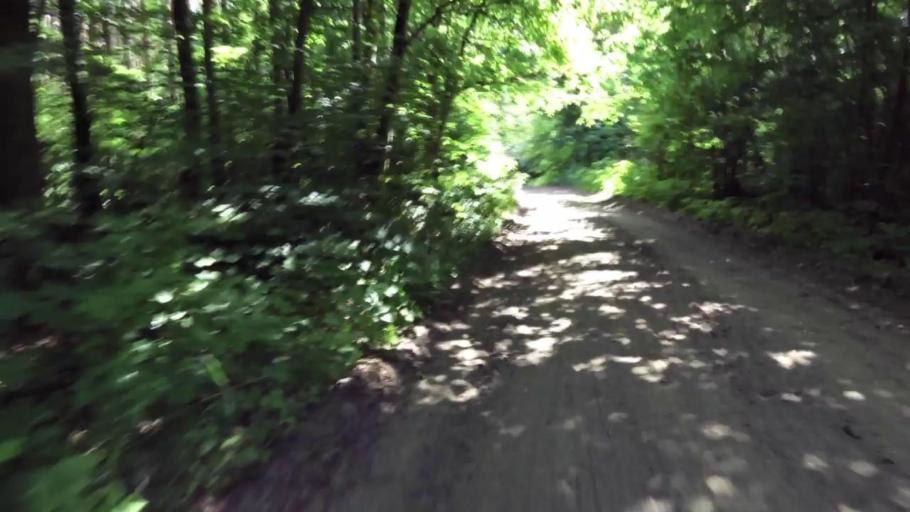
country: PL
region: West Pomeranian Voivodeship
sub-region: Powiat kamienski
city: Miedzyzdroje
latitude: 53.9317
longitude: 14.5343
